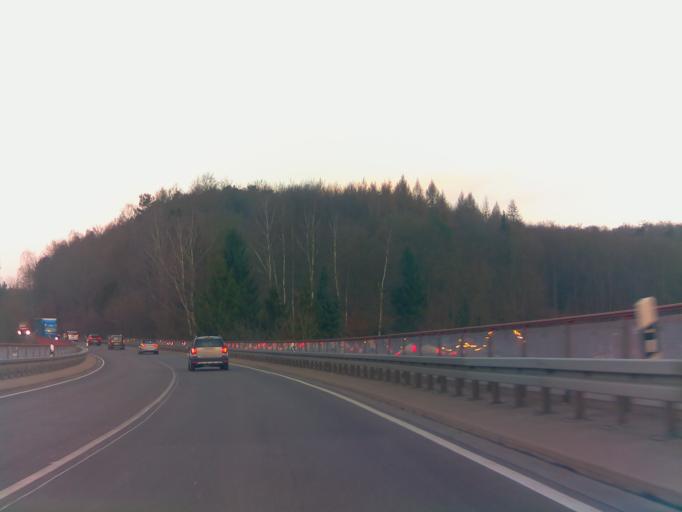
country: DE
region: Saarland
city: Sankt Ingbert
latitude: 49.2676
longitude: 7.0852
